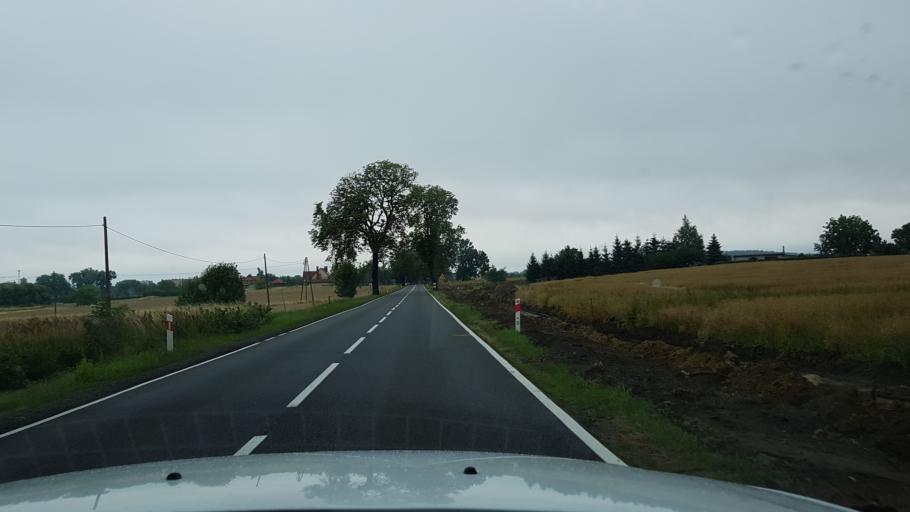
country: PL
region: West Pomeranian Voivodeship
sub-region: Powiat mysliborski
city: Mysliborz
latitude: 52.9237
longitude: 14.8413
